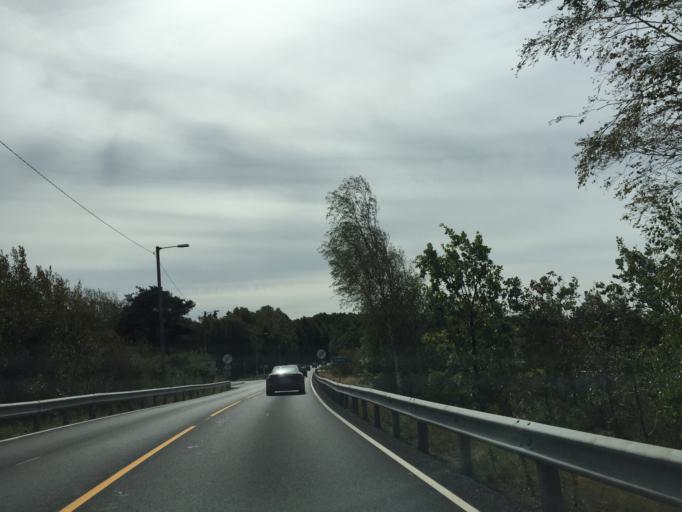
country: NO
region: Ostfold
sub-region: Fredrikstad
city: Fredrikstad
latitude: 59.1442
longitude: 10.9467
